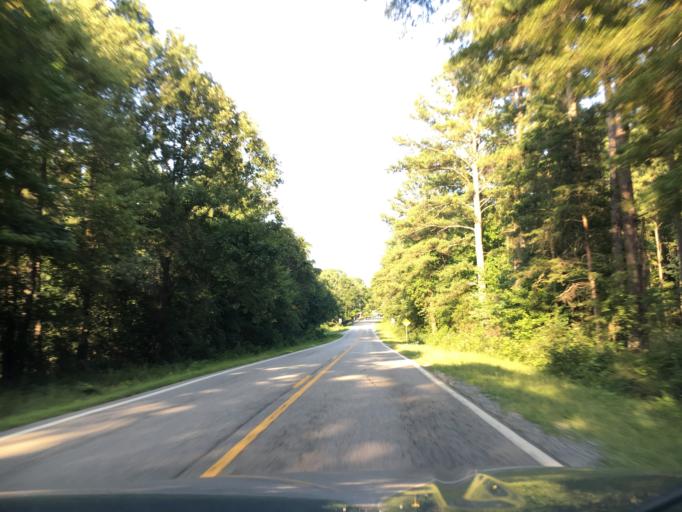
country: US
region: Virginia
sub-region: Pittsylvania County
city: Chatham
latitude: 36.8284
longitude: -79.2854
